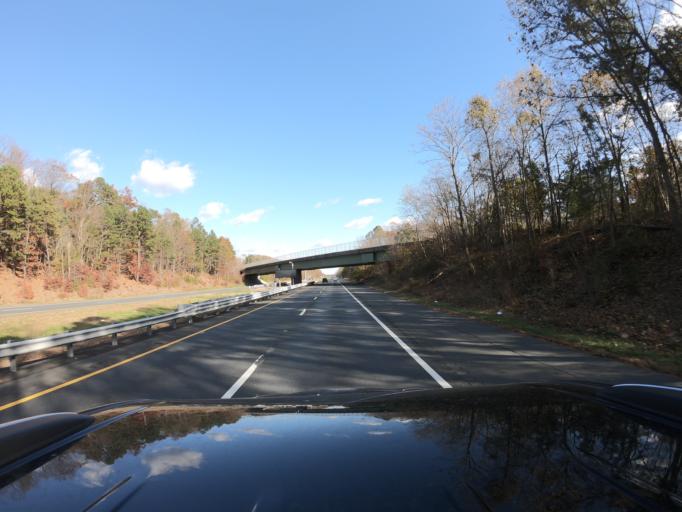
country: US
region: New Jersey
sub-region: Monmouth County
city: Farmingdale
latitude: 40.1669
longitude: -74.2086
